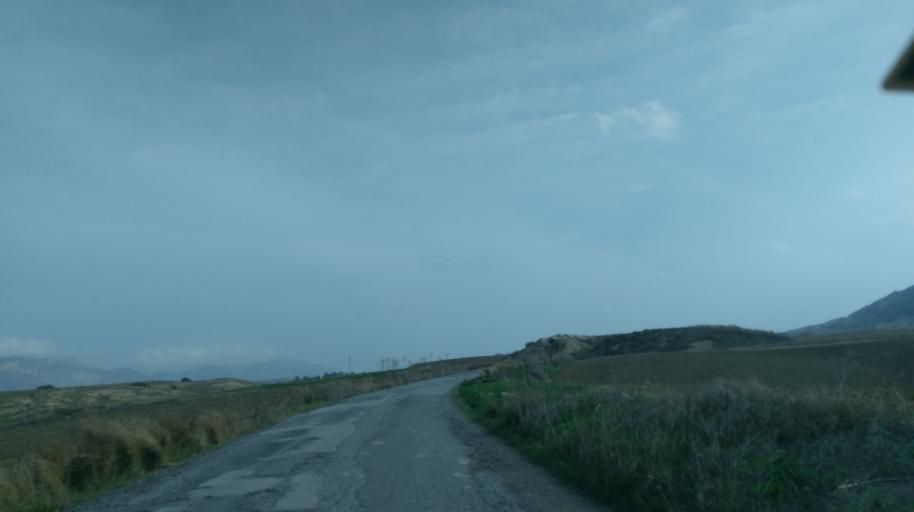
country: CY
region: Keryneia
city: Lapithos
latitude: 35.2623
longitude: 33.1043
